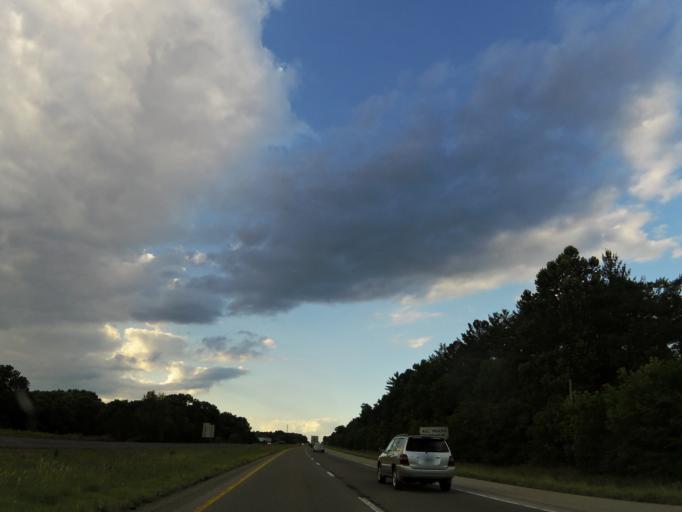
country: US
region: Tennessee
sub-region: Maury County
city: Spring Hill
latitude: 35.6667
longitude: -86.8917
